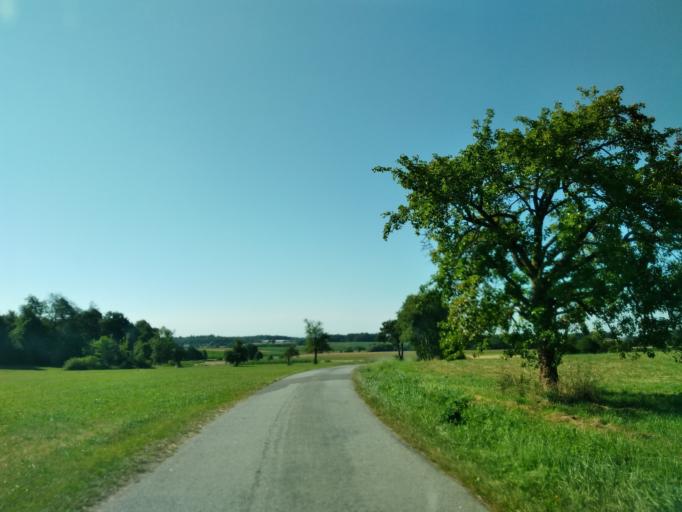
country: DE
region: Baden-Wuerttemberg
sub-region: Karlsruhe Region
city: Limbach
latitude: 49.4769
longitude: 9.2450
